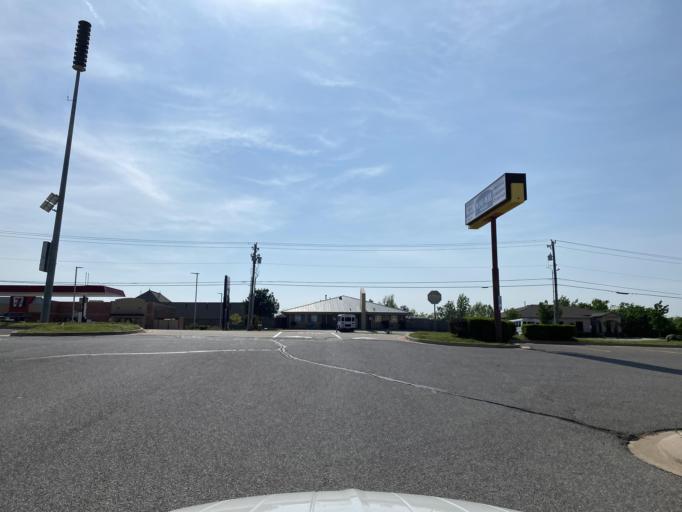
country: US
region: Oklahoma
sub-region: Oklahoma County
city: Midwest City
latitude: 35.4506
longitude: -97.3527
